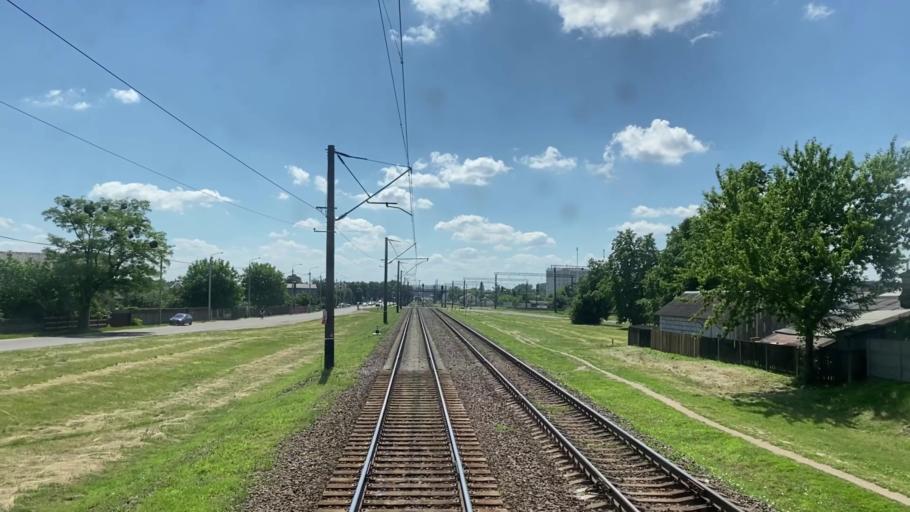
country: BY
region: Brest
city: Baranovichi
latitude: 53.1385
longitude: 26.0323
